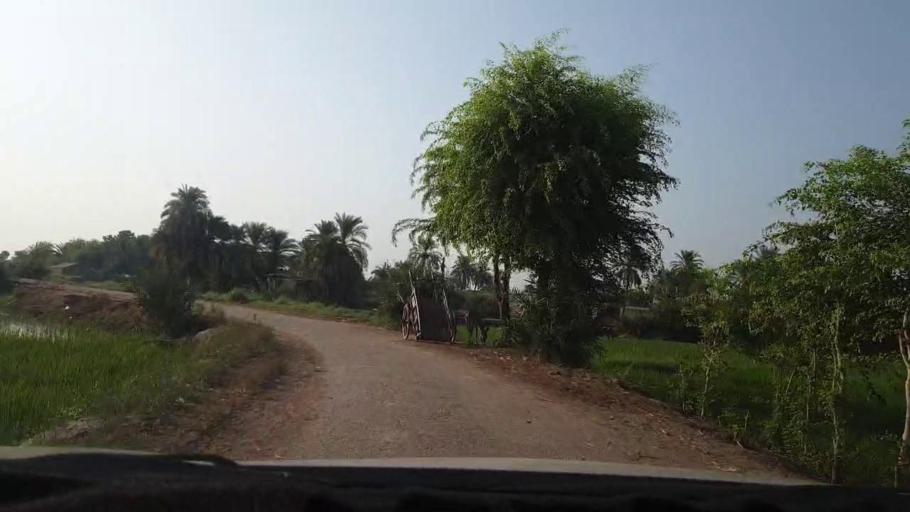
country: PK
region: Sindh
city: Larkana
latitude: 27.5125
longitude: 68.1788
